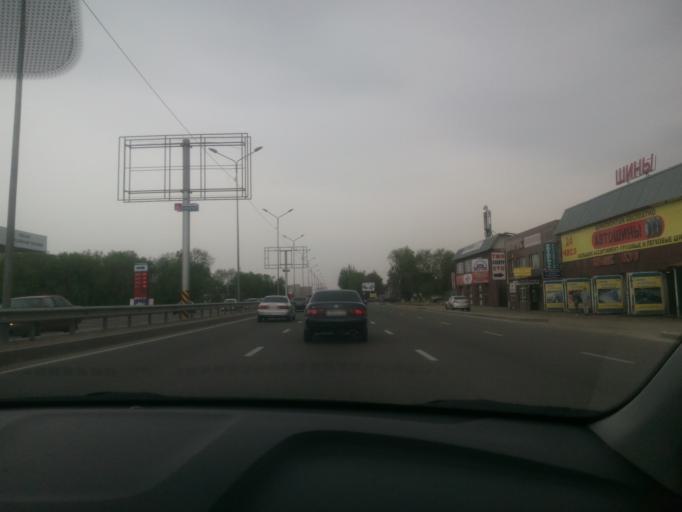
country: KZ
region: Almaty Qalasy
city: Almaty
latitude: 43.2375
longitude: 76.8079
